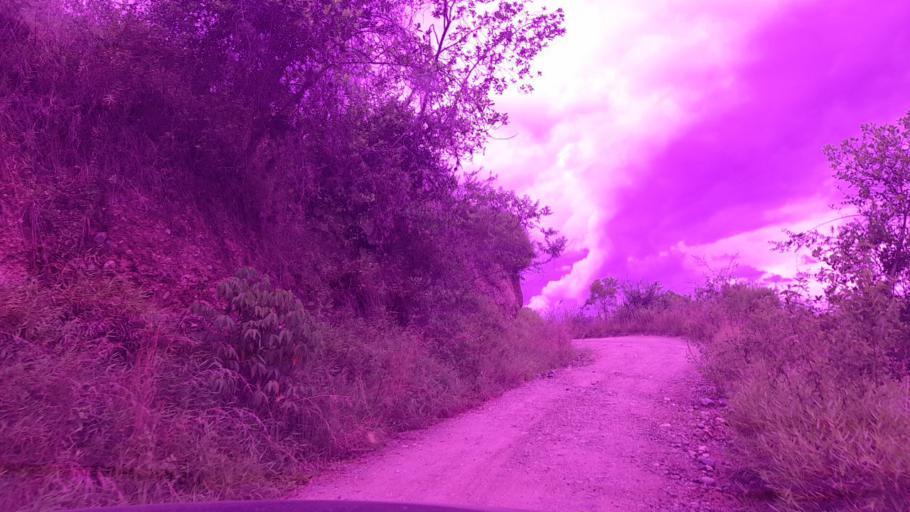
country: CO
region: Valle del Cauca
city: Andalucia
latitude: 4.1716
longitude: -76.1218
